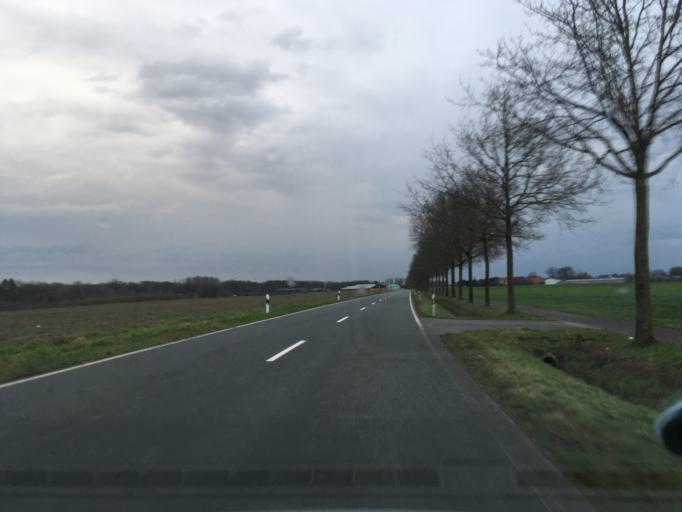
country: DE
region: North Rhine-Westphalia
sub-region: Regierungsbezirk Munster
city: Schoppingen
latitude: 52.0704
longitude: 7.2395
